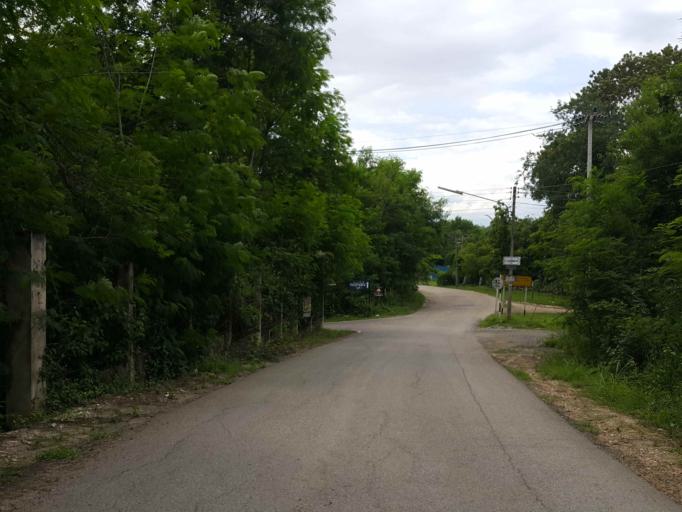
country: TH
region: Chiang Mai
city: San Sai
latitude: 18.9270
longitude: 98.9219
